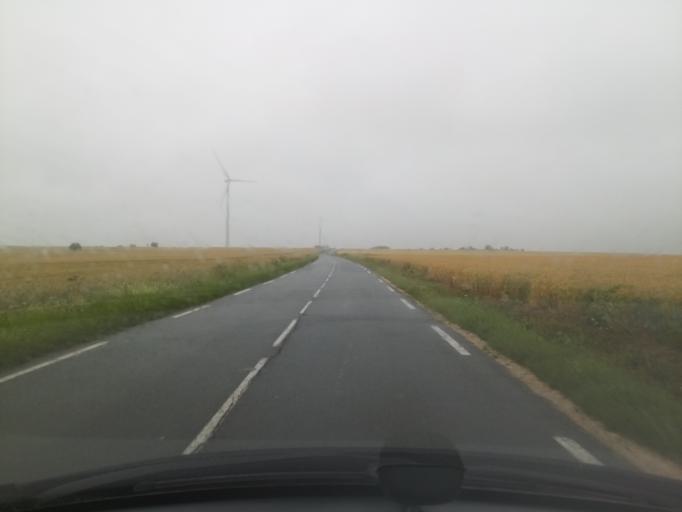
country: FR
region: Poitou-Charentes
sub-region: Departement de la Charente-Maritime
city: Saint-Jean-de-Liversay
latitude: 46.2457
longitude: -0.8814
